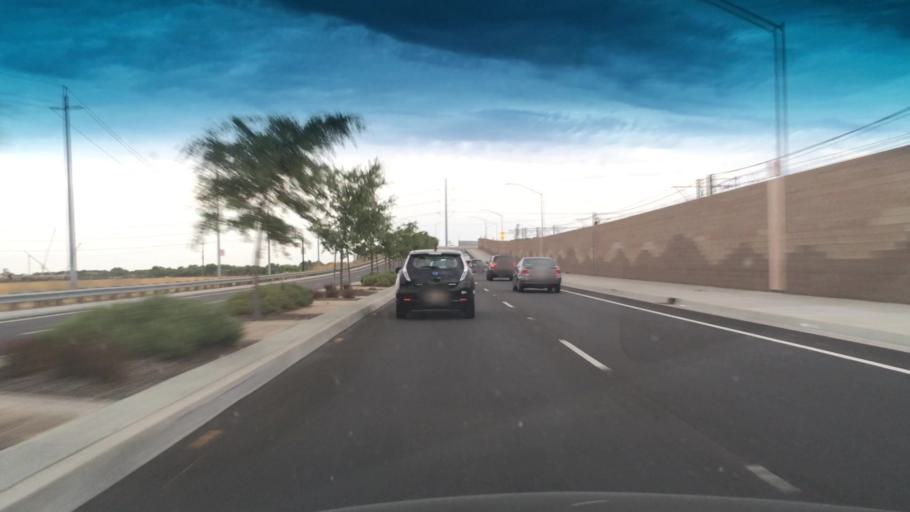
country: US
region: California
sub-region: Sacramento County
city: Parkway
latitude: 38.4616
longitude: -121.4561
